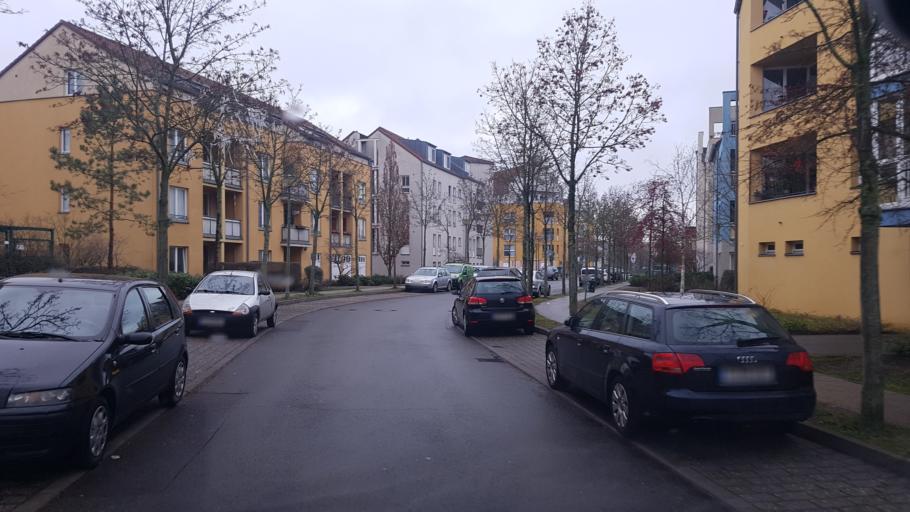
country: DE
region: Berlin
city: Wannsee
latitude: 52.3637
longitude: 13.1348
